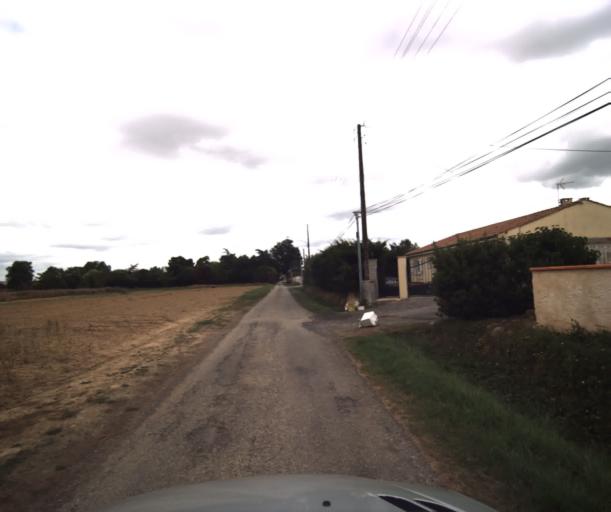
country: FR
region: Midi-Pyrenees
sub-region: Departement de la Haute-Garonne
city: Labarthe-sur-Leze
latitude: 43.4629
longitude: 1.3939
